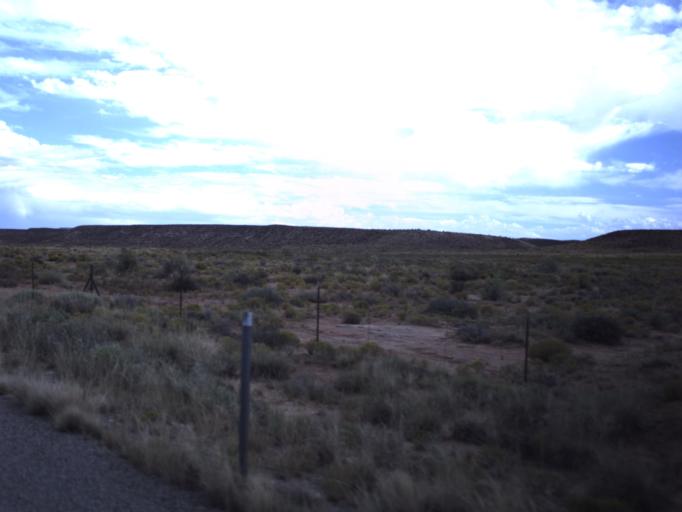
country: US
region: Utah
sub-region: San Juan County
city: Blanding
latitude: 37.2916
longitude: -109.4169
